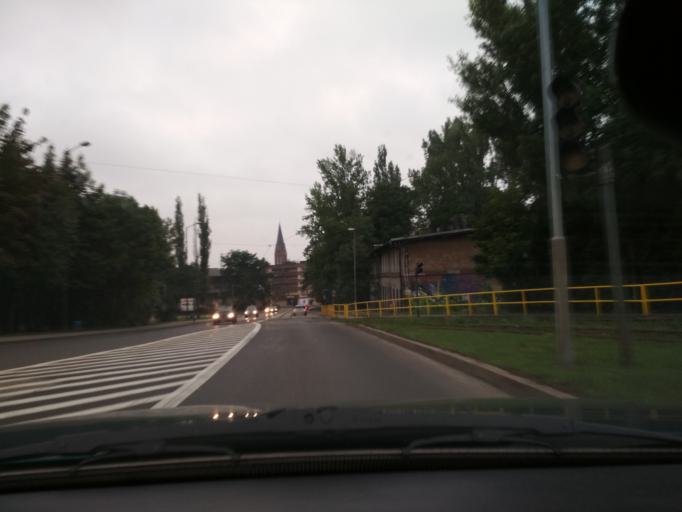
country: PL
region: Silesian Voivodeship
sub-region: Swietochlowice
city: Swietochlowice
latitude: 50.2953
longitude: 18.9169
